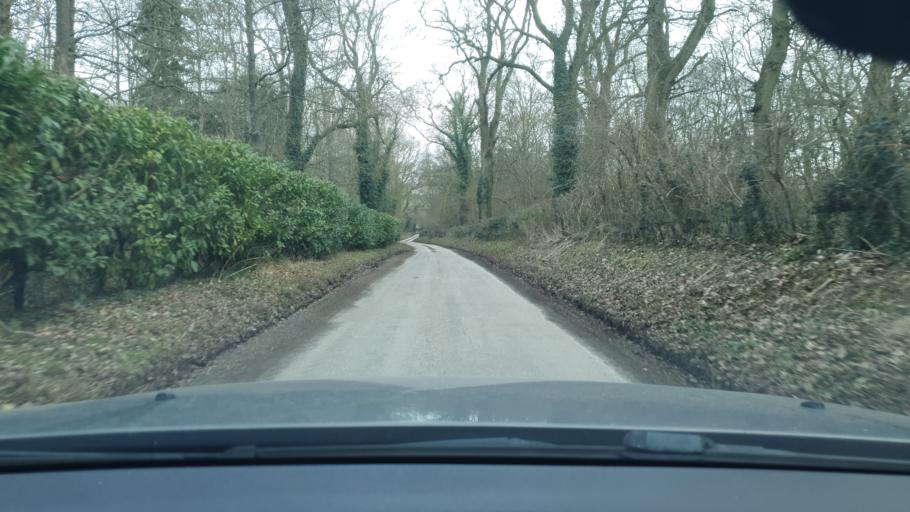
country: GB
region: England
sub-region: West Berkshire
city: Hungerford
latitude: 51.3679
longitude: -1.4999
